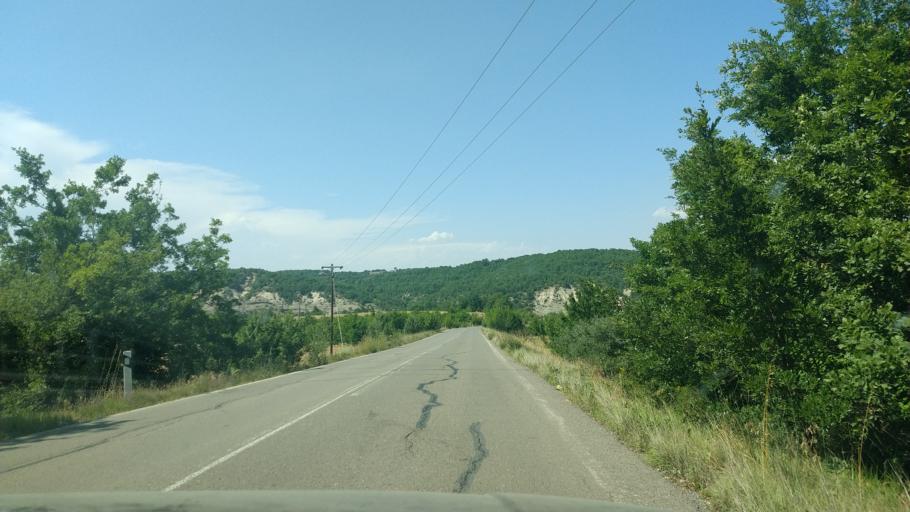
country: GR
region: West Macedonia
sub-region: Nomos Grevenon
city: Grevena
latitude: 40.0451
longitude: 21.4820
